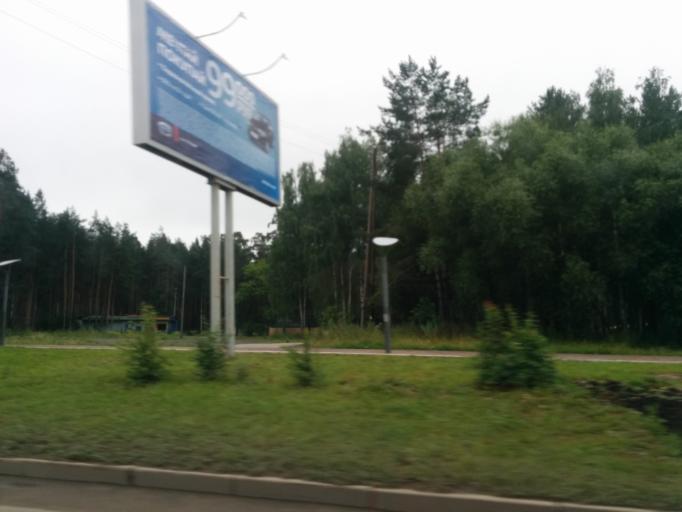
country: RU
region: Perm
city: Kondratovo
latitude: 57.9935
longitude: 56.1780
